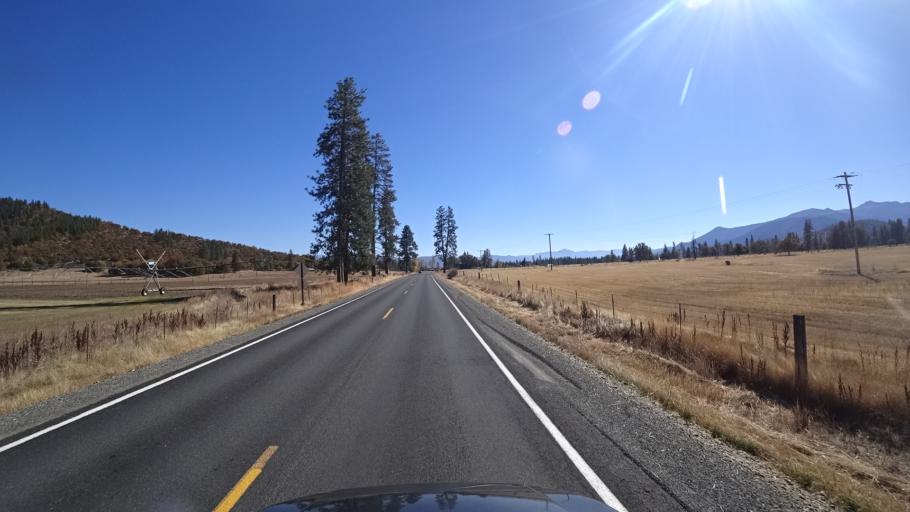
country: US
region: California
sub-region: Siskiyou County
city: Yreka
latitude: 41.5575
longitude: -122.9223
